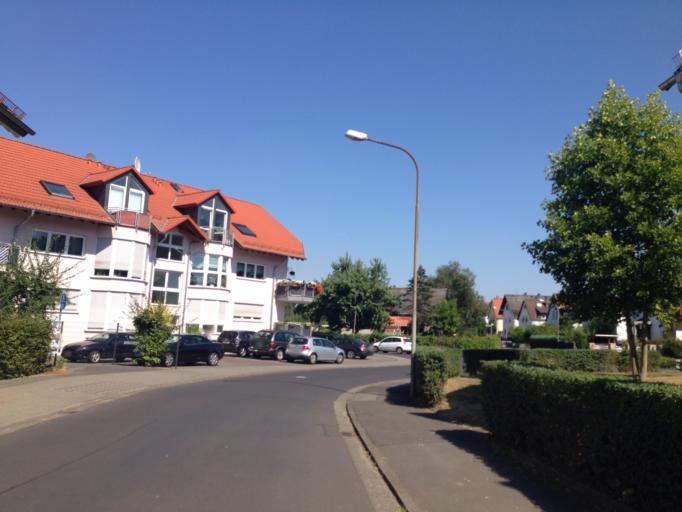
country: DE
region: Hesse
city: Lollar
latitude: 50.6457
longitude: 8.7055
